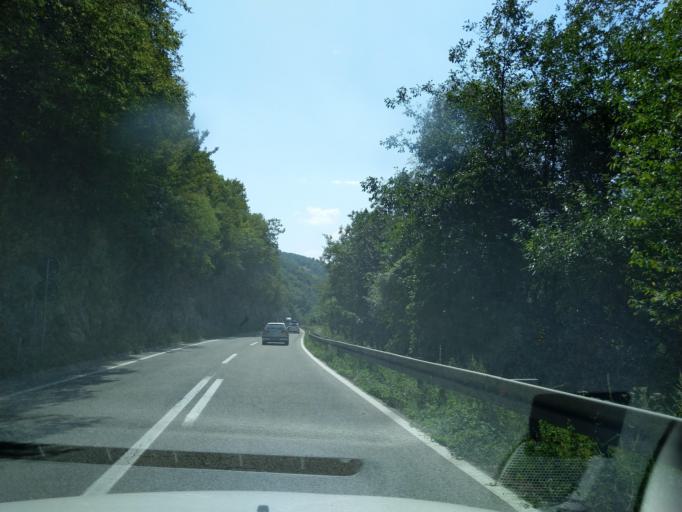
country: RS
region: Central Serbia
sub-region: Zlatiborski Okrug
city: Prijepolje
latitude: 43.4644
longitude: 19.6471
